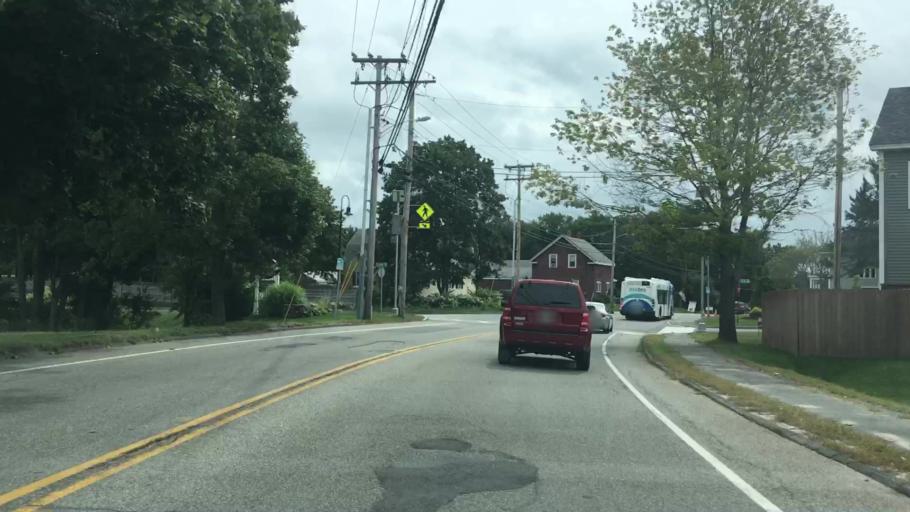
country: US
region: Maine
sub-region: Cumberland County
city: Westbrook
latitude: 43.6663
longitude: -70.3590
